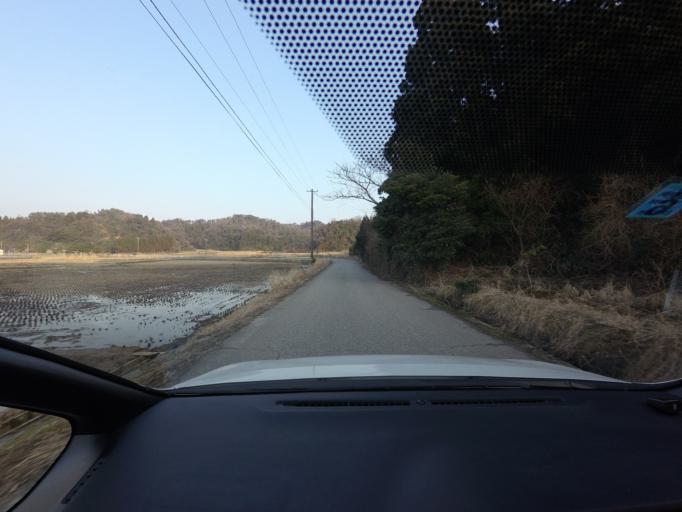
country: JP
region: Ishikawa
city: Nanao
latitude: 37.1404
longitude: 137.0120
